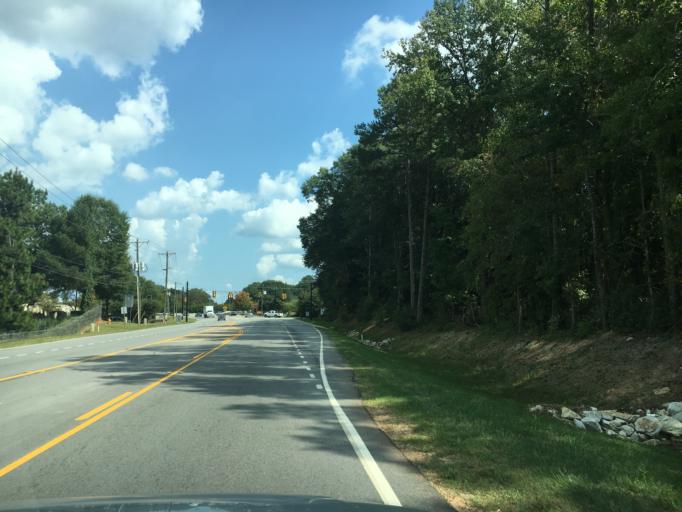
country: US
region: South Carolina
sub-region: Greenville County
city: Mauldin
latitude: 34.8356
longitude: -82.2850
